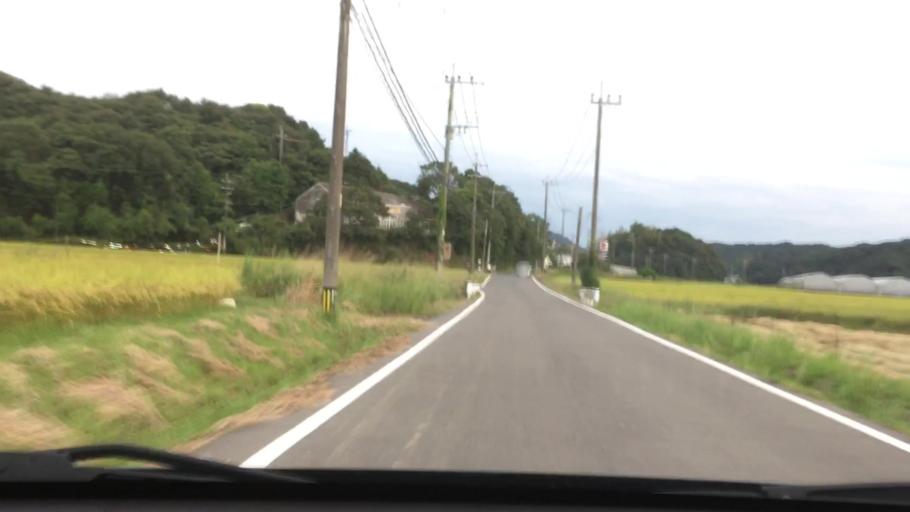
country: JP
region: Nagasaki
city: Sasebo
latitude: 32.9962
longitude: 129.7688
